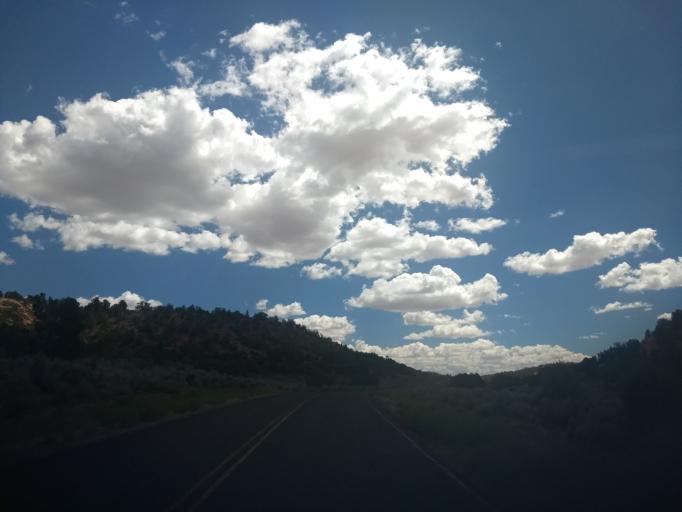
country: US
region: Utah
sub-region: Kane County
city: Kanab
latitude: 37.1128
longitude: -112.6779
